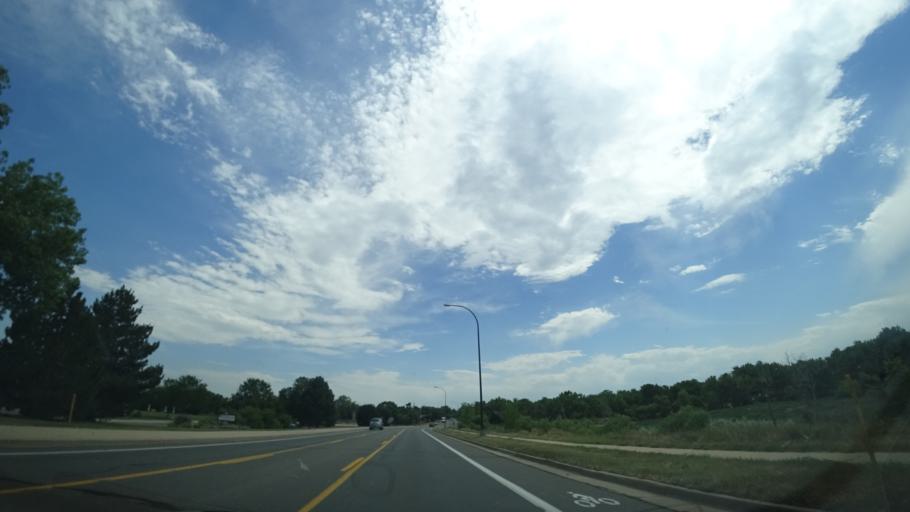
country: US
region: Colorado
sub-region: Jefferson County
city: Lakewood
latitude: 39.6914
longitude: -105.1005
